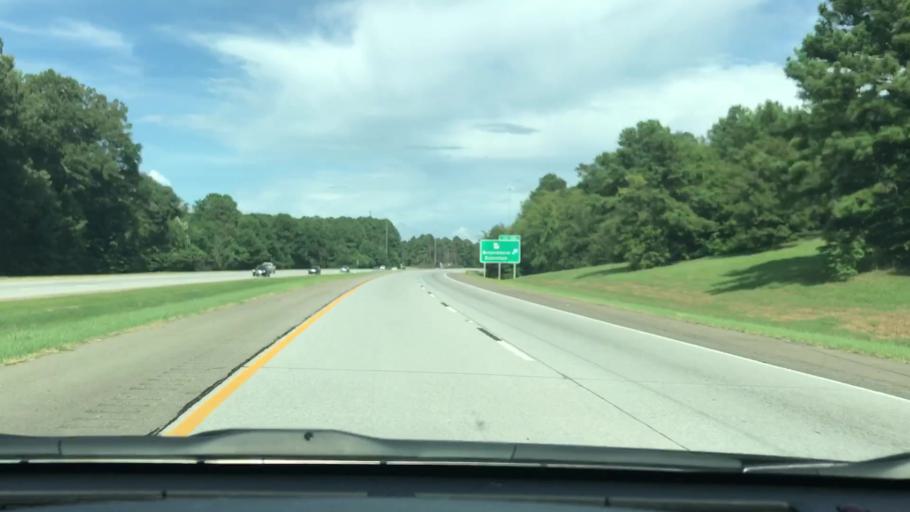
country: US
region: Georgia
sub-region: Greene County
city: Greensboro
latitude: 33.5447
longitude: -83.2145
